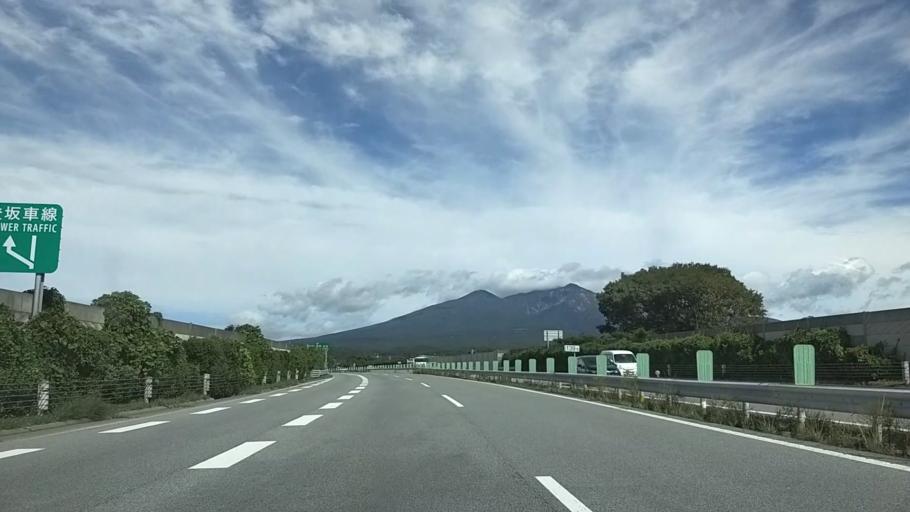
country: JP
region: Yamanashi
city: Nirasaki
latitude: 35.8326
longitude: 138.3920
